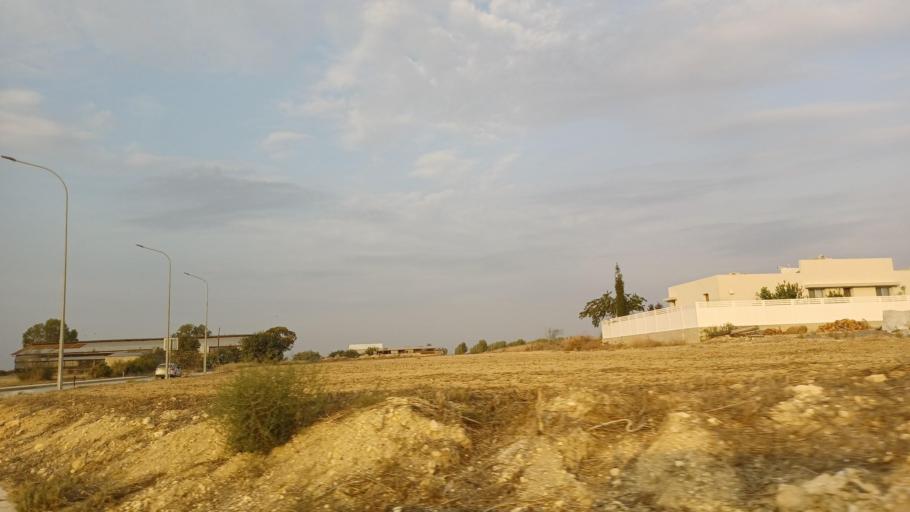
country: CY
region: Larnaka
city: Athienou
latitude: 35.0619
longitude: 33.5279
